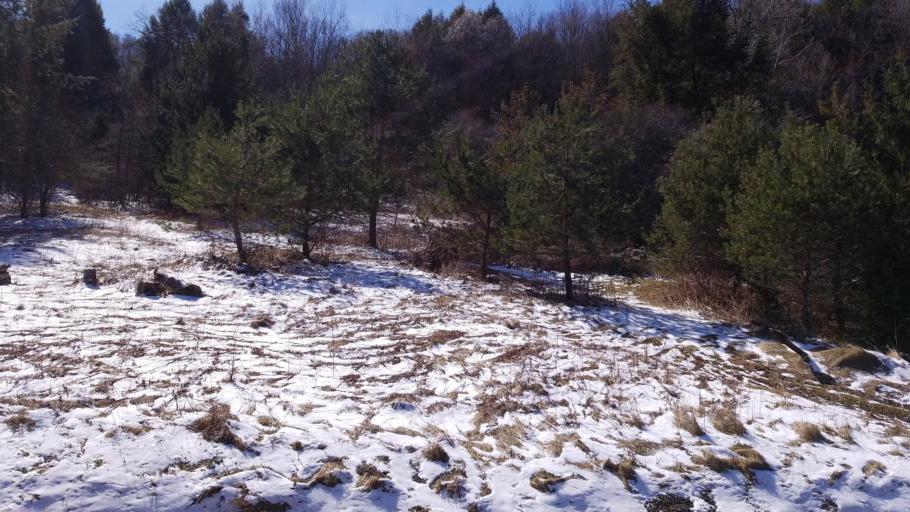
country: US
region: New York
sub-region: Allegany County
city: Wellsville
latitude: 41.9630
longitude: -77.8452
